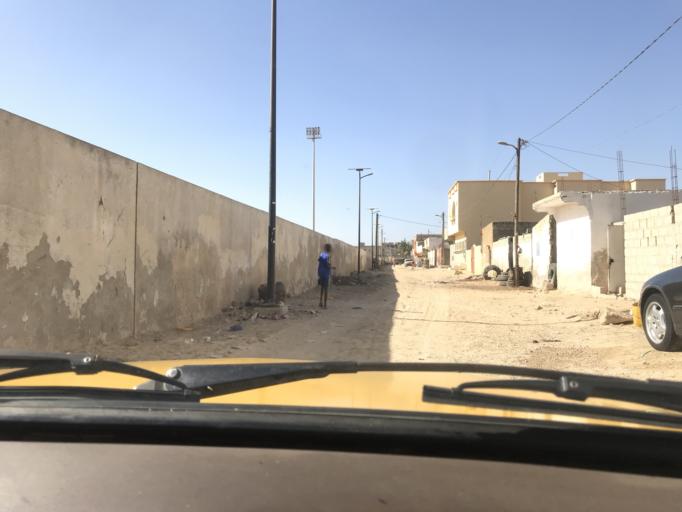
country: SN
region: Saint-Louis
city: Saint-Louis
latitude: 16.0078
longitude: -16.4869
